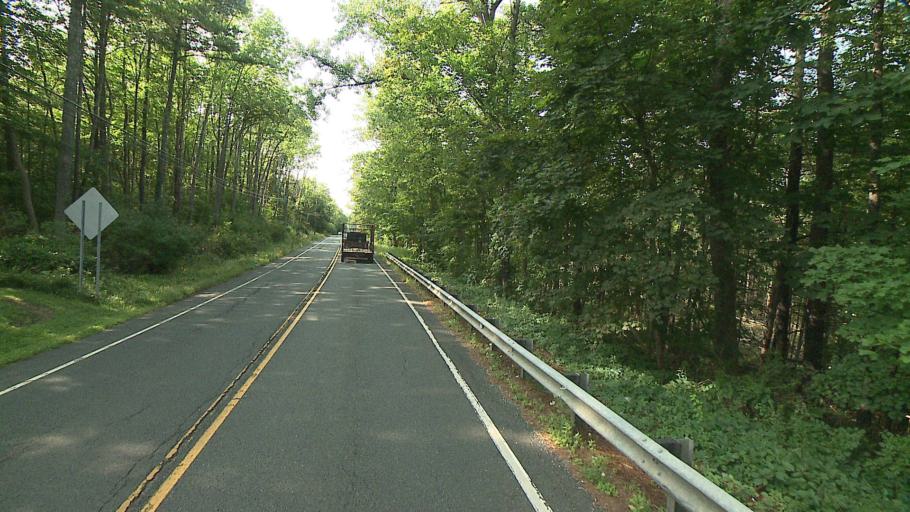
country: US
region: Connecticut
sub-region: Litchfield County
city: Canaan
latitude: 41.9514
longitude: -73.3600
